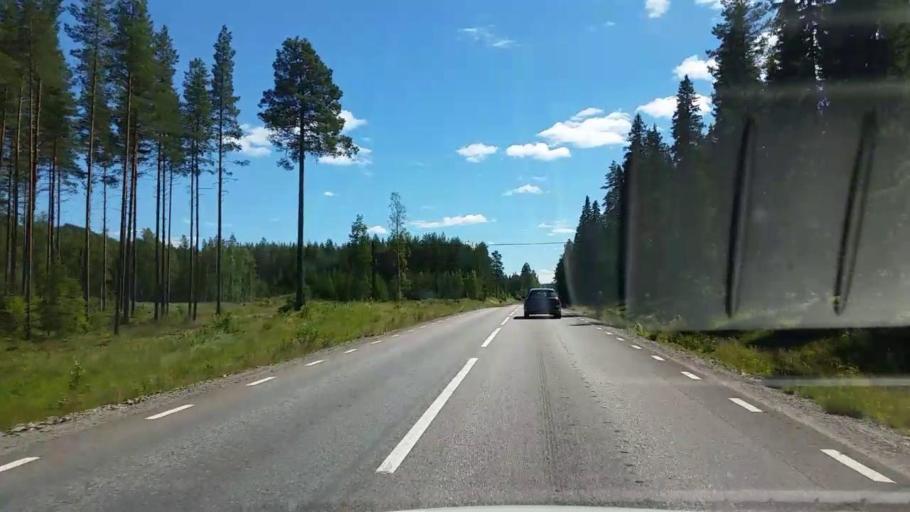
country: SE
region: Gaevleborg
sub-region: Ovanakers Kommun
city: Edsbyn
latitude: 61.1938
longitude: 15.8745
